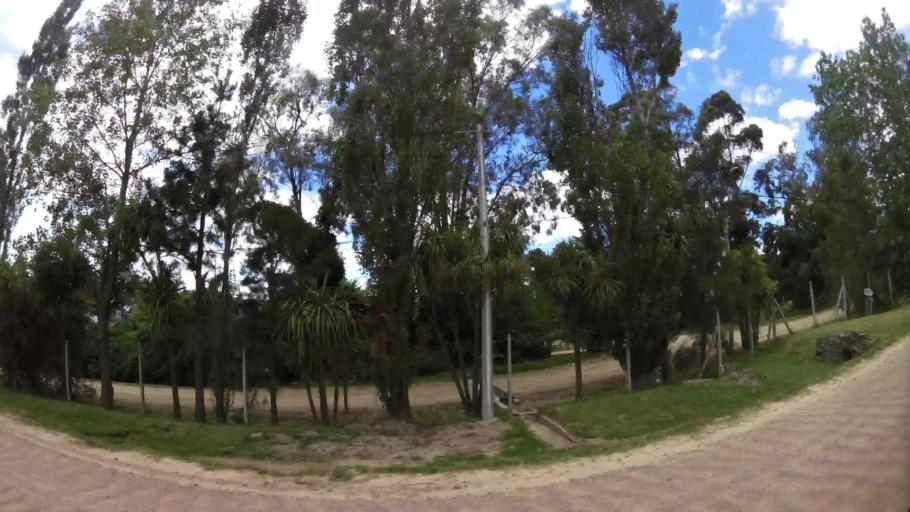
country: UY
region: Canelones
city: Colonia Nicolich
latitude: -34.8201
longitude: -55.9904
